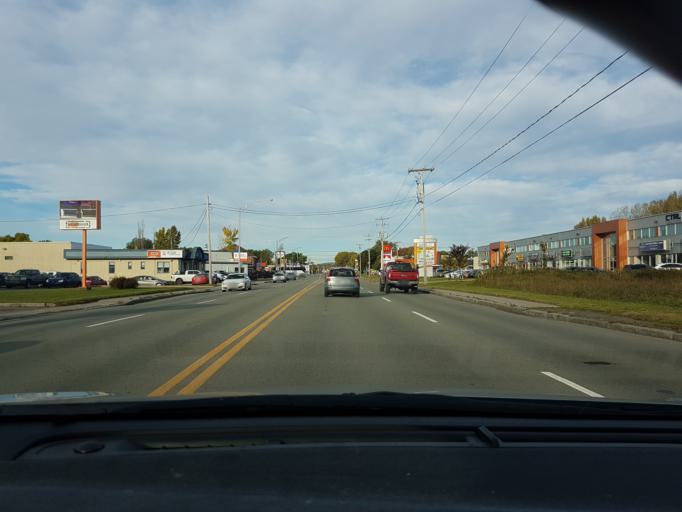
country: CA
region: Quebec
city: L'Ancienne-Lorette
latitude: 46.8063
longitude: -71.3125
